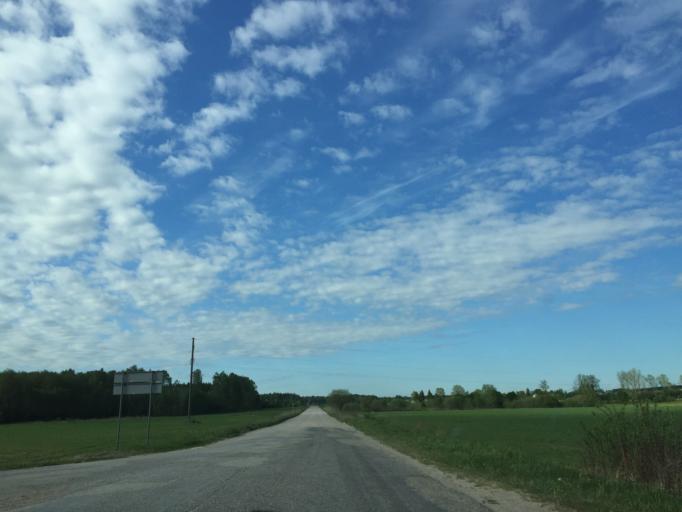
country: LV
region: Lecava
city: Iecava
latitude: 56.6061
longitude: 24.0721
